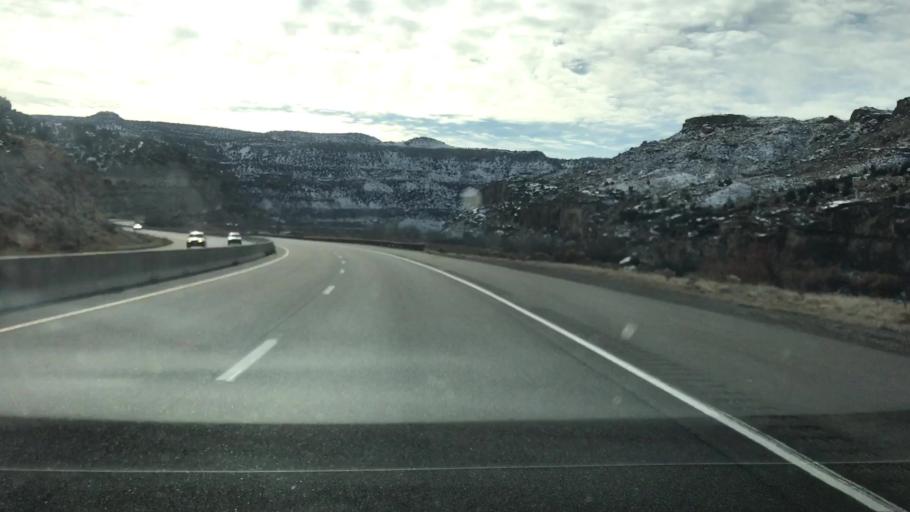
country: US
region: Colorado
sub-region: Mesa County
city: Palisade
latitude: 39.2545
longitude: -108.2597
